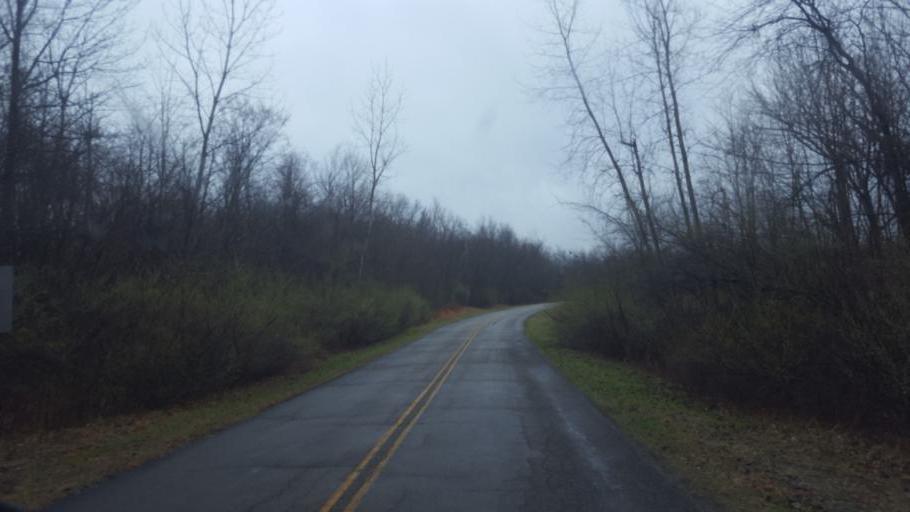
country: US
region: Ohio
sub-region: Delaware County
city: Lewis Center
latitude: 40.2008
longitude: -82.9805
